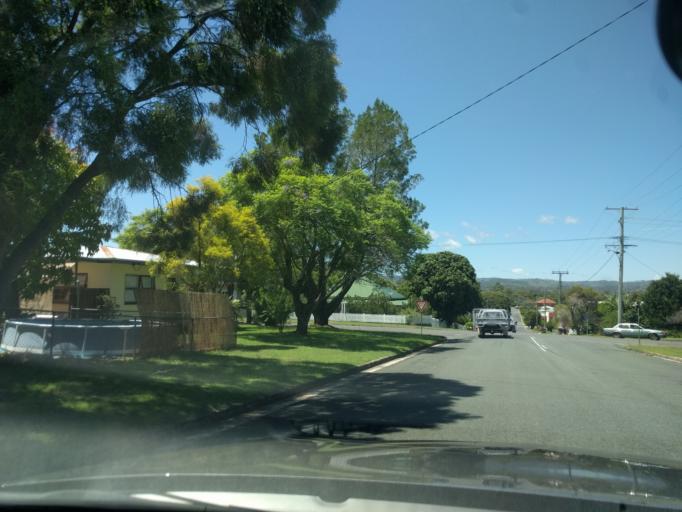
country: AU
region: Queensland
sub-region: Logan
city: Cedar Vale
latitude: -27.9867
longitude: 153.0007
